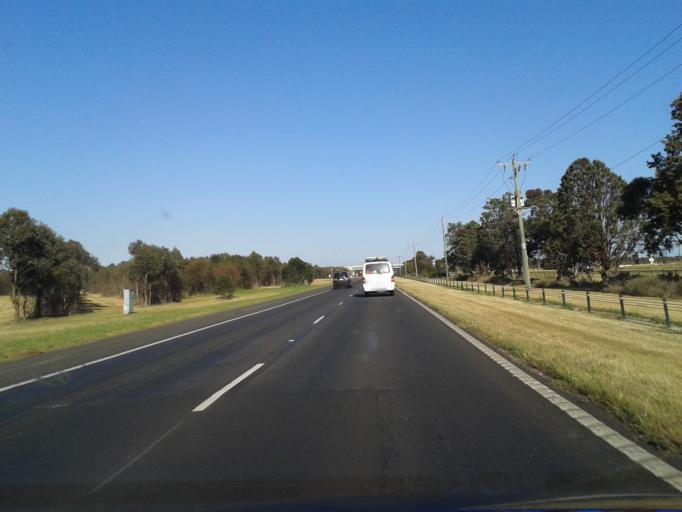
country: AU
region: Victoria
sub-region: Melton
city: Rockbank
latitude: -37.7431
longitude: 144.6956
